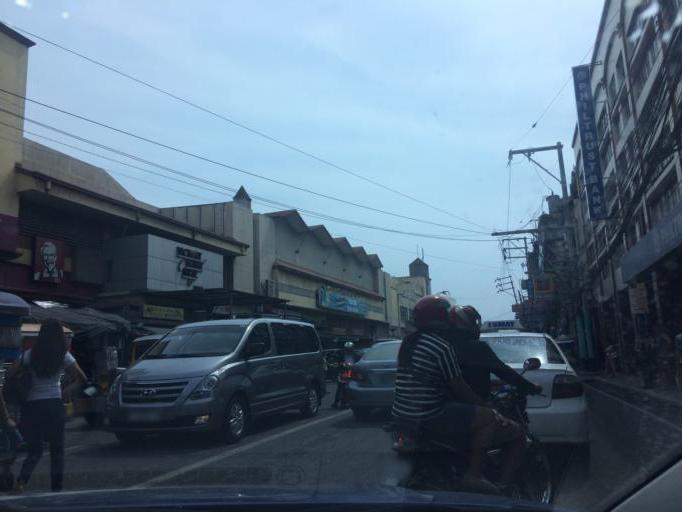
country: PH
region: Metro Manila
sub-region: Makati City
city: Makati City
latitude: 14.5477
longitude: 120.9985
